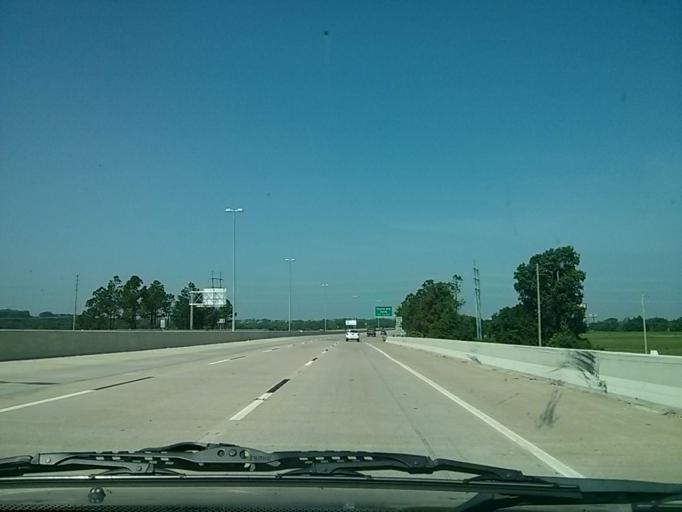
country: US
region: Oklahoma
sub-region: Tulsa County
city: Jenks
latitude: 36.0177
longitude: -95.9551
